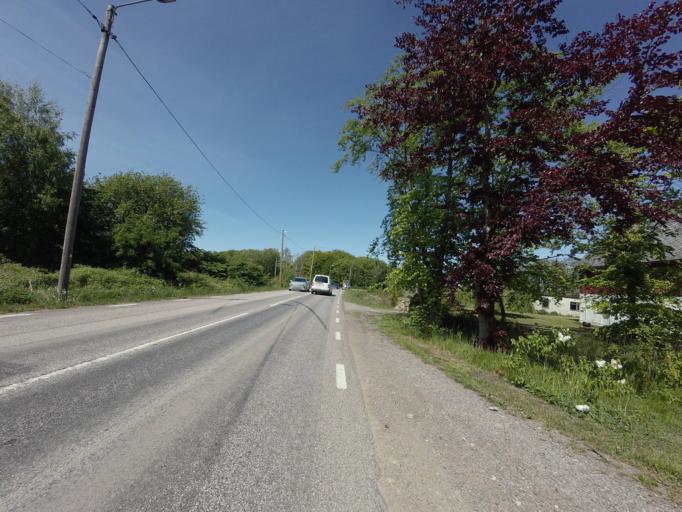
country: SE
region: Skane
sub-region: Helsingborg
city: Odakra
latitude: 56.1485
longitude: 12.6784
